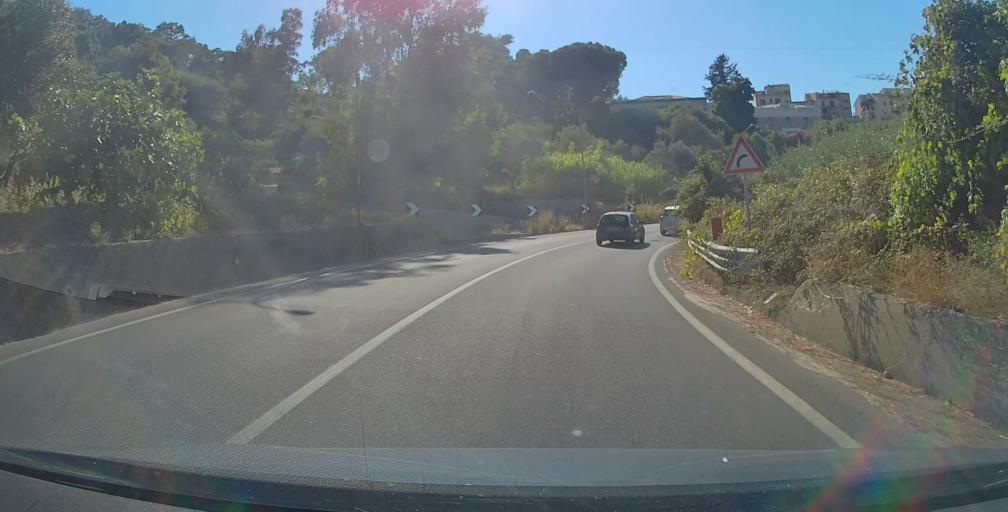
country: IT
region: Sicily
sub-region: Messina
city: Capo d'Orlando
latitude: 38.1539
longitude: 14.7529
